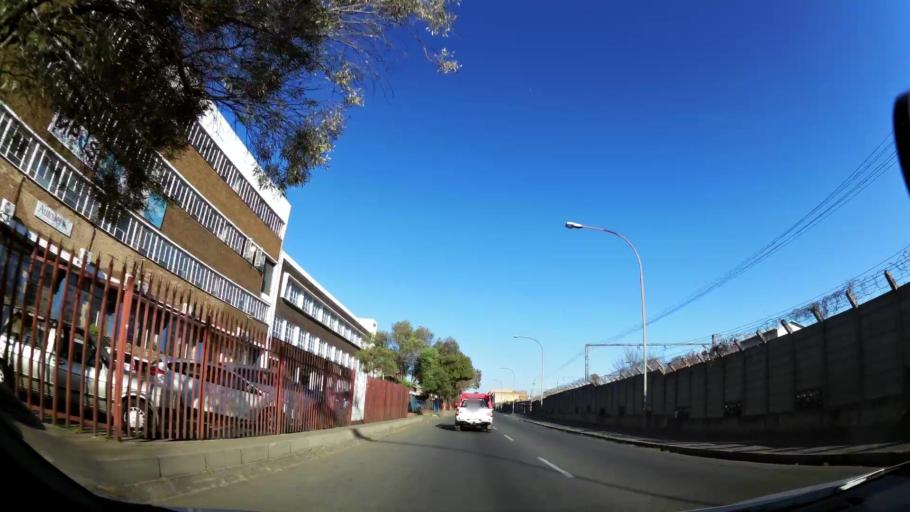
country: ZA
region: Gauteng
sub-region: City of Johannesburg Metropolitan Municipality
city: Johannesburg
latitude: -26.2077
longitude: 28.0813
